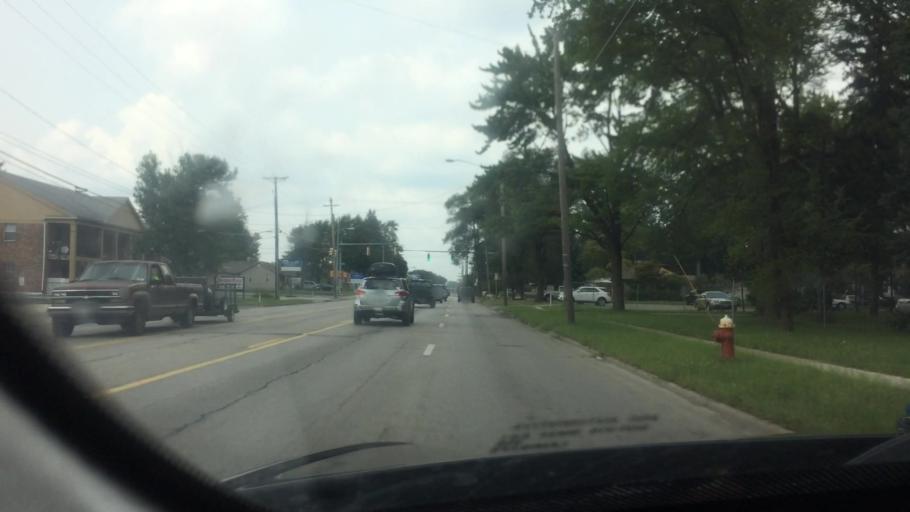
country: US
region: Ohio
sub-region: Lucas County
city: Ottawa Hills
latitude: 41.7124
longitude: -83.6238
